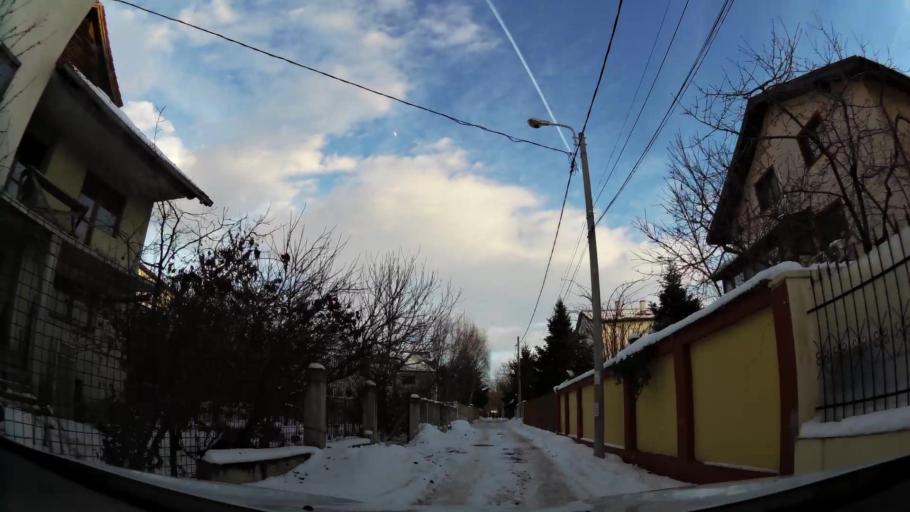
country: RO
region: Ilfov
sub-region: Comuna Popesti-Leordeni
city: Popesti-Leordeni
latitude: 44.3775
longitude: 26.1257
